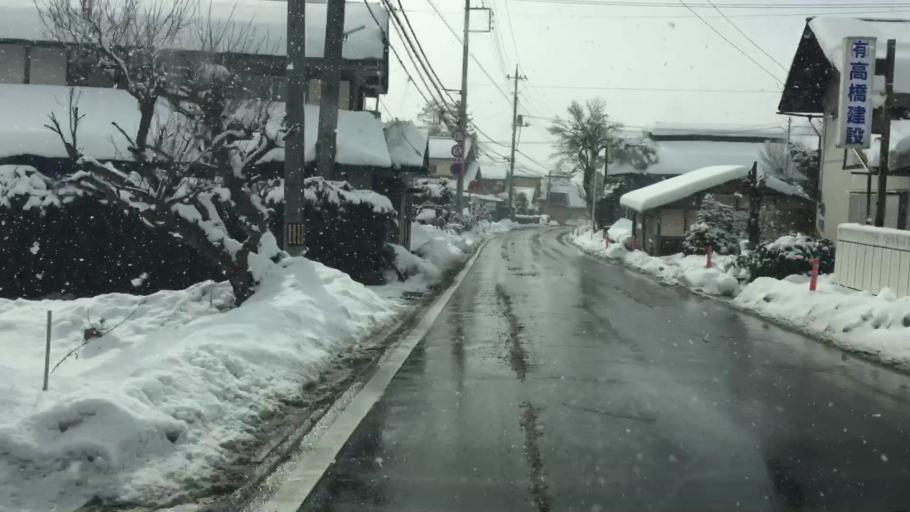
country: JP
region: Gunma
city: Numata
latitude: 36.6974
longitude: 139.0648
